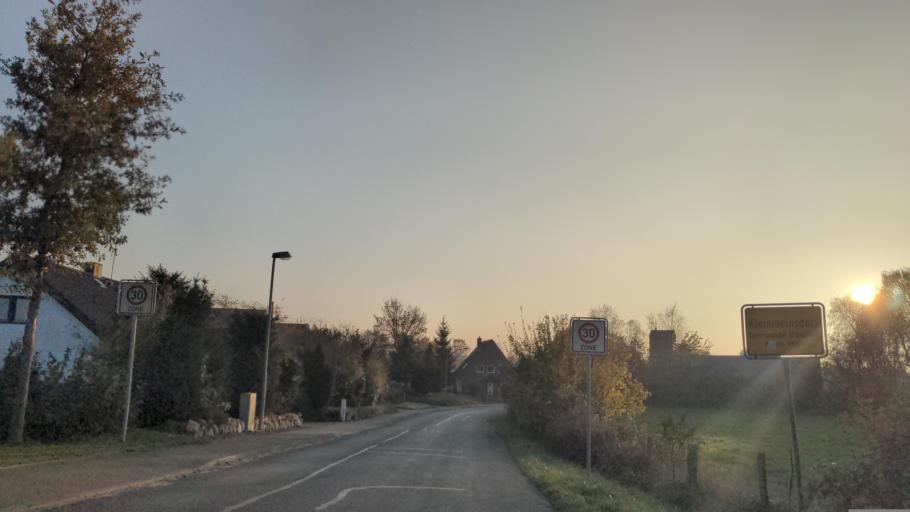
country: DE
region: Schleswig-Holstein
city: Bosdorf
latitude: 54.1324
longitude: 10.5045
